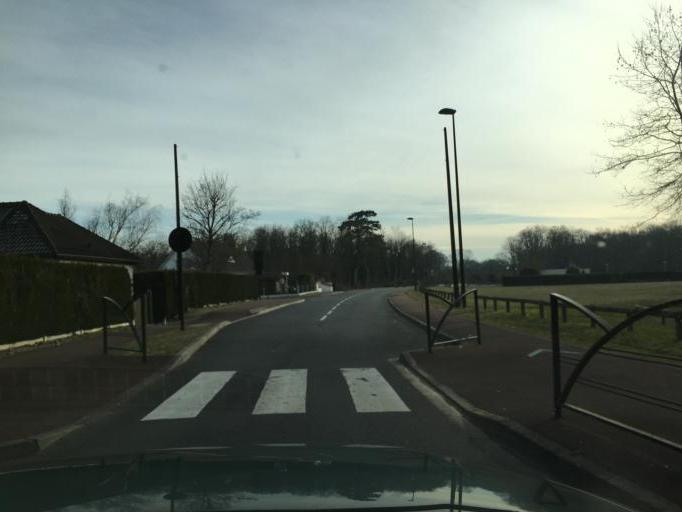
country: FR
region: Centre
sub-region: Departement du Loiret
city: Saint-Cyr-en-Val
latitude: 47.8262
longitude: 1.9710
